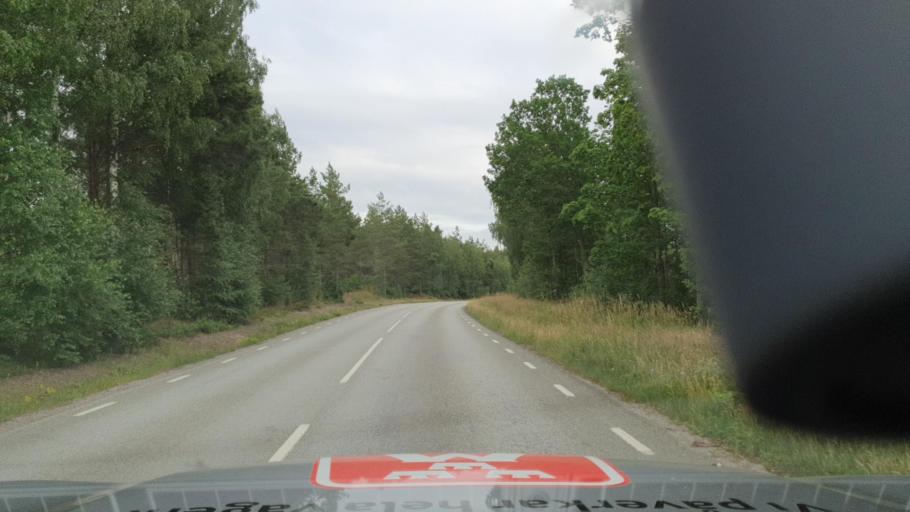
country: SE
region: Kalmar
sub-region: Kalmar Kommun
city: Trekanten
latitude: 56.6612
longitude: 16.0050
